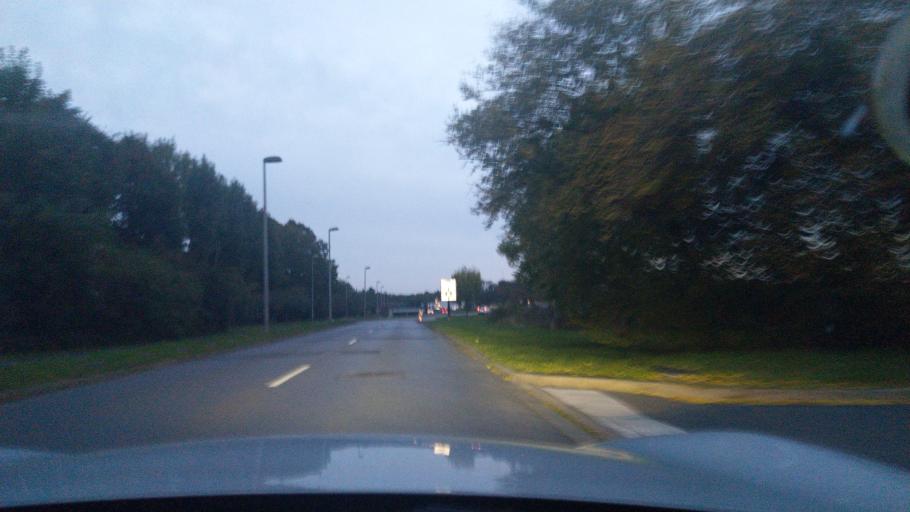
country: FR
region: Ile-de-France
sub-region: Departement de Seine-et-Marne
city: Emerainville
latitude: 48.8170
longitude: 2.6286
